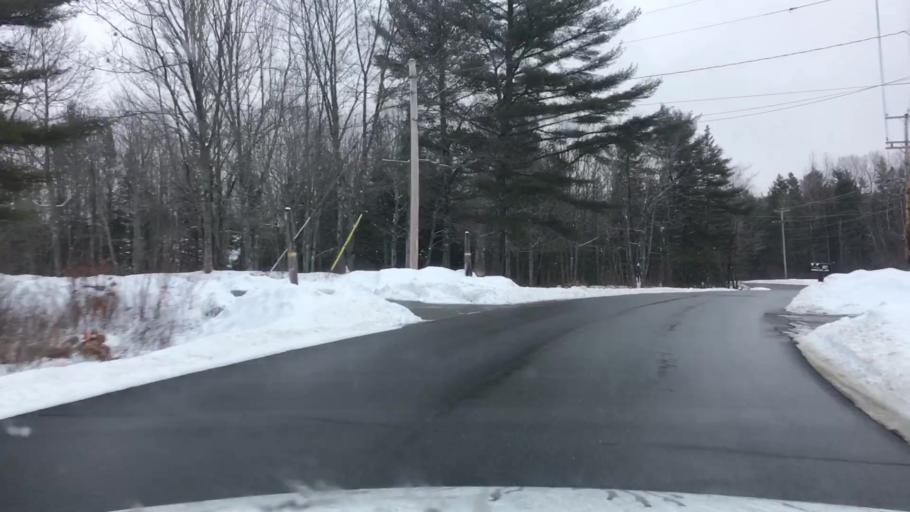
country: US
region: Maine
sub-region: Hancock County
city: Trenton
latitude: 44.4072
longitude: -68.3225
